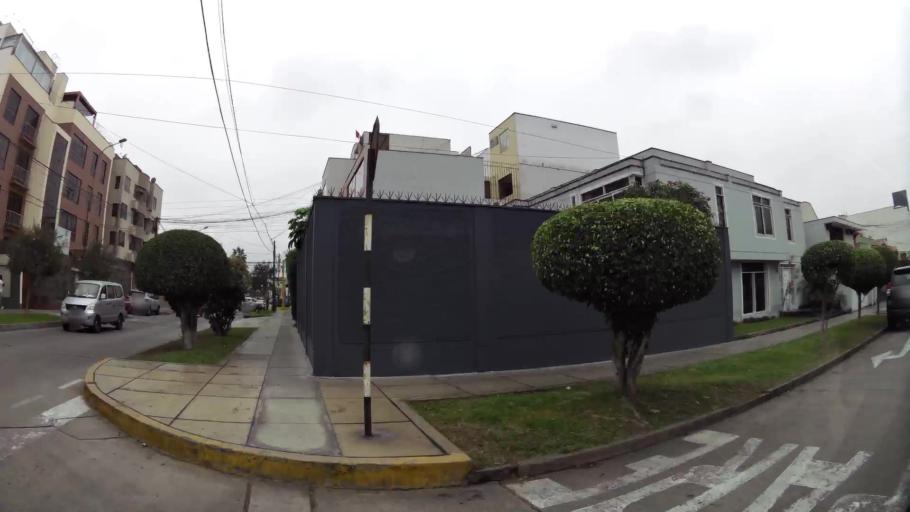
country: PE
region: Lima
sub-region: Lima
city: Surco
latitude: -12.1305
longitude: -77.0101
